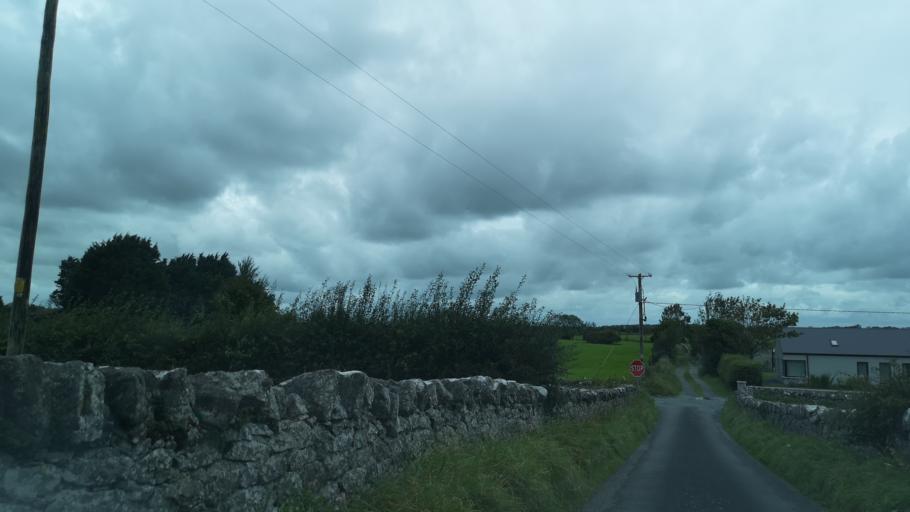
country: IE
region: Connaught
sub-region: County Galway
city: Athenry
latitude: 53.3136
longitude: -8.7469
